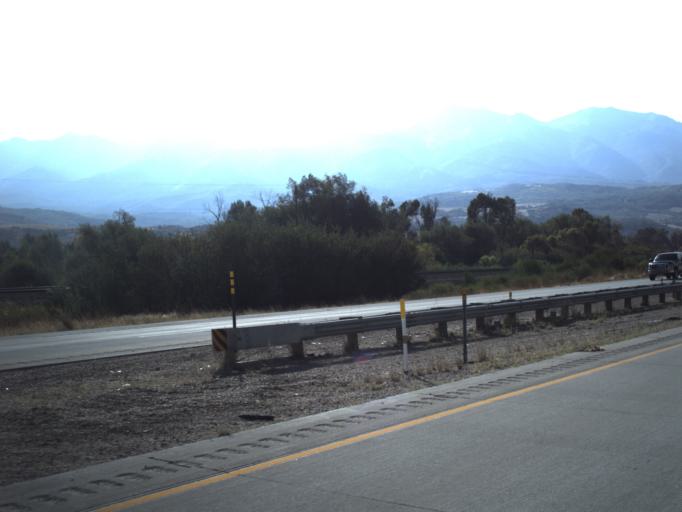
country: US
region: Utah
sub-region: Morgan County
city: Mountain Green
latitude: 41.1112
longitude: -111.7548
